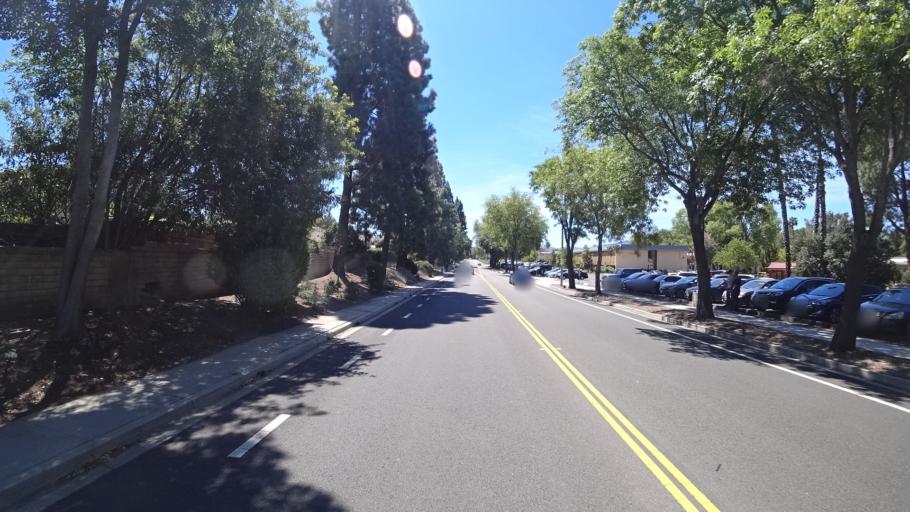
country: US
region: California
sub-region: Ventura County
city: Moorpark
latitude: 34.2242
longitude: -118.8757
